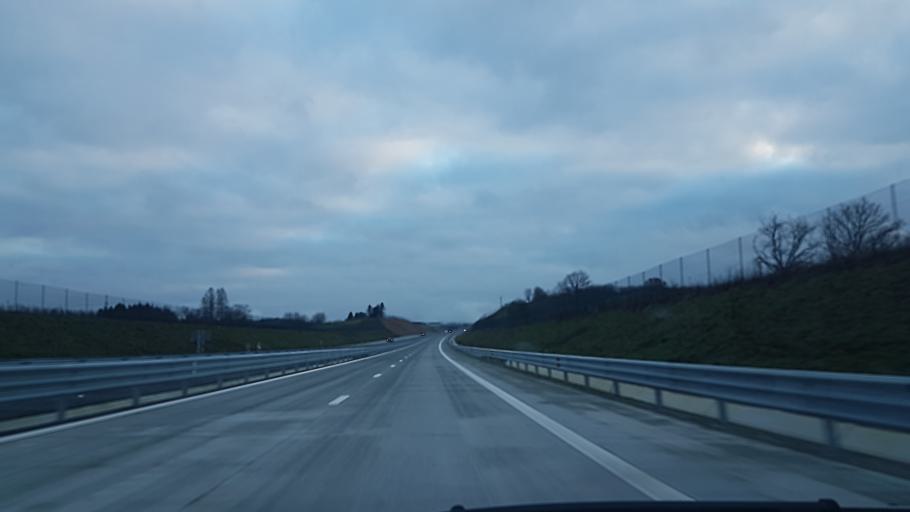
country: FR
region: Champagne-Ardenne
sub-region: Departement des Ardennes
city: Rocroi
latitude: 49.9738
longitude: 4.5383
